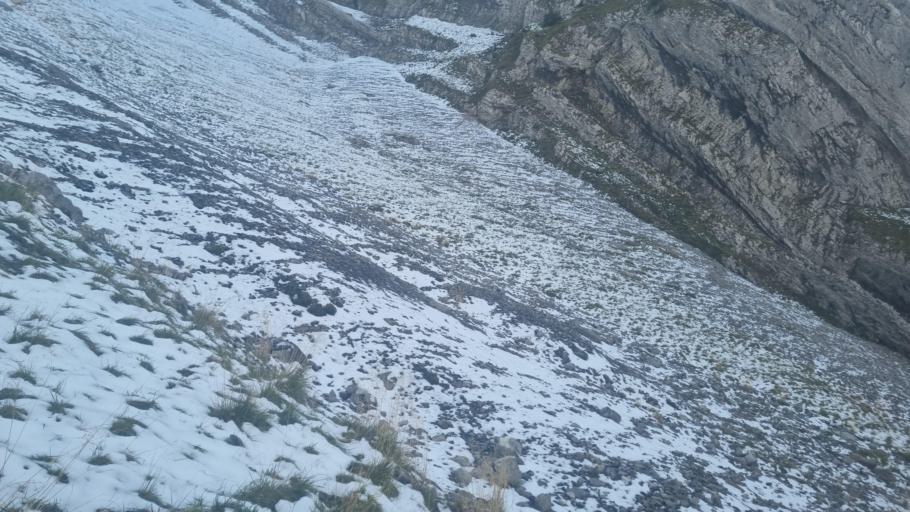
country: CH
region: Schwyz
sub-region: Bezirk March
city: Vorderthal
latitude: 47.0975
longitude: 8.9542
